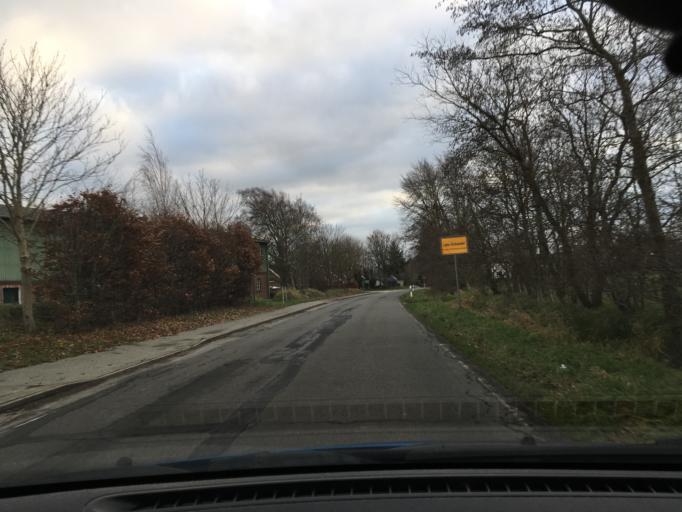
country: DE
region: Schleswig-Holstein
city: Lohe-Rickelshof
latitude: 54.1847
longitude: 9.0610
